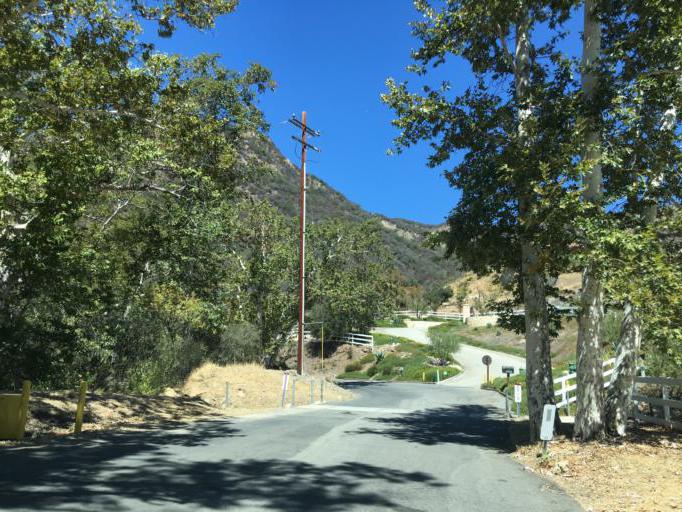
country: US
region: California
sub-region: Los Angeles County
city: Westlake Village
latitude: 34.1187
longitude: -118.8160
